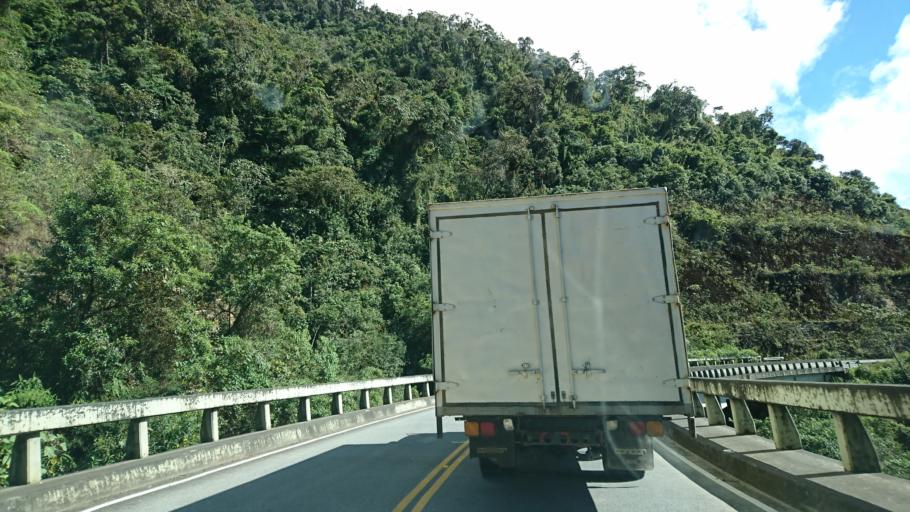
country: BO
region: La Paz
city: Coroico
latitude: -16.2209
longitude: -67.8220
